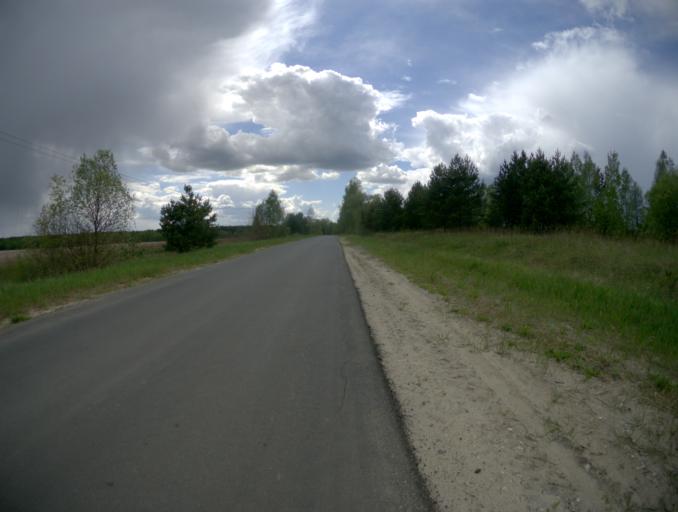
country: RU
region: Vladimir
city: Velikodvorskiy
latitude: 55.2578
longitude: 40.7816
